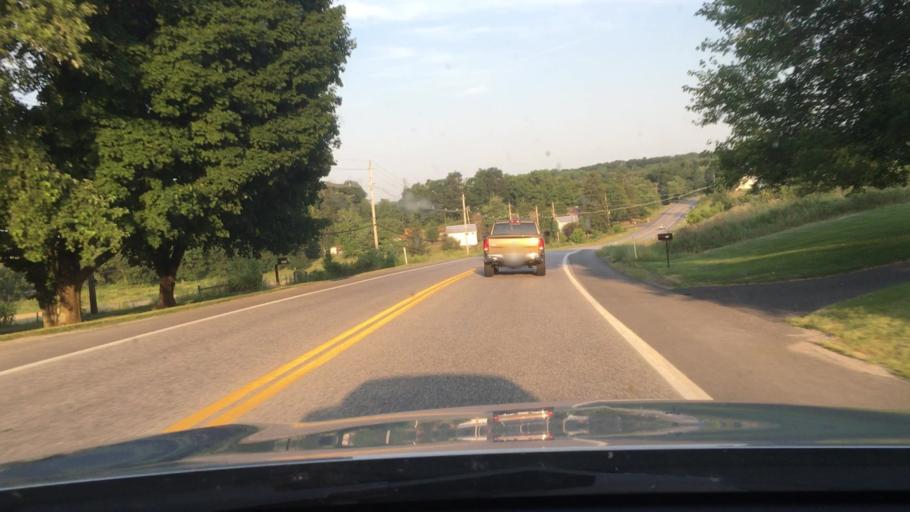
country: US
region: Pennsylvania
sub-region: York County
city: Dillsburg
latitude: 40.0798
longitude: -76.9317
